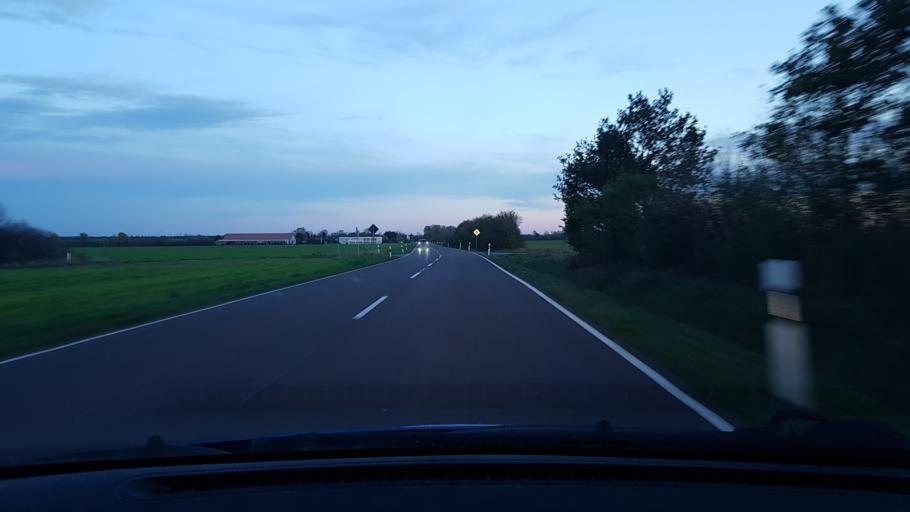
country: DE
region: Saxony-Anhalt
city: Leitzkau
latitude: 52.0257
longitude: 12.0005
